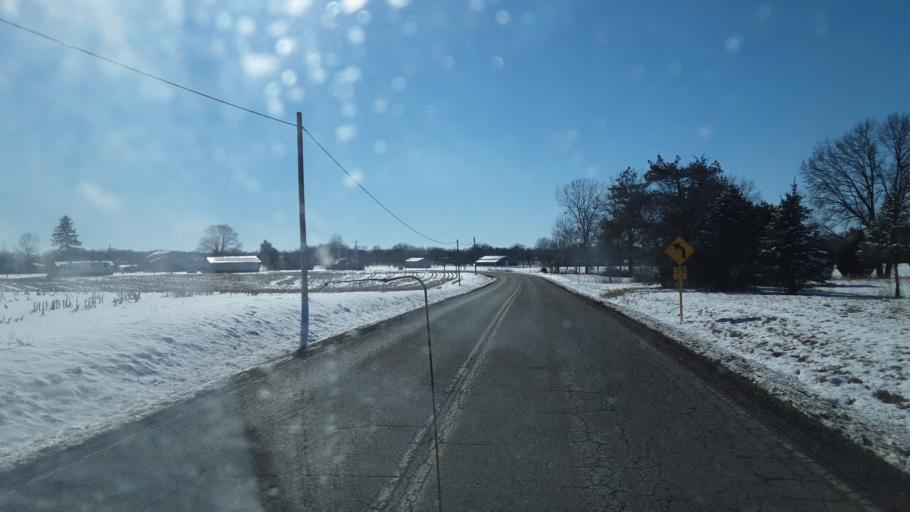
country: US
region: Ohio
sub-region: Licking County
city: Hebron
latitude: 39.9679
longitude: -82.4592
